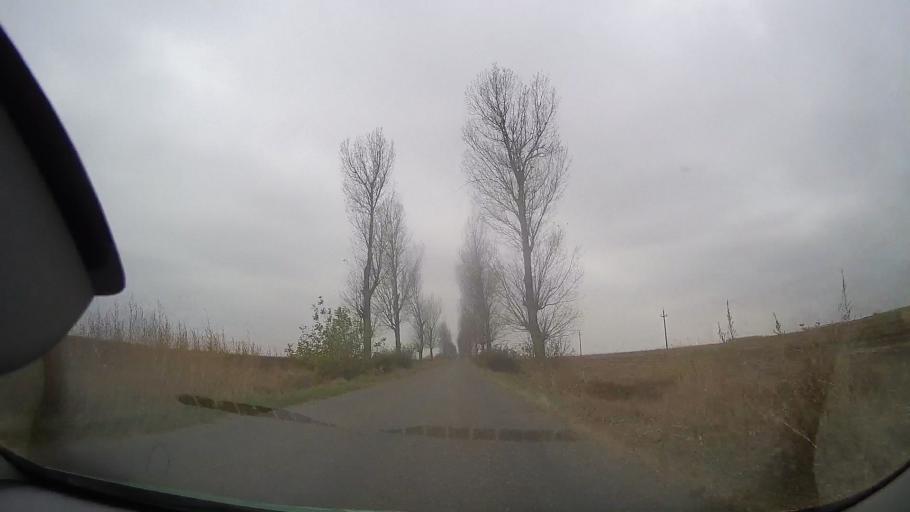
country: RO
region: Buzau
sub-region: Comuna Scutelnici
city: Scutelnici
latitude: 44.8430
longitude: 26.8759
